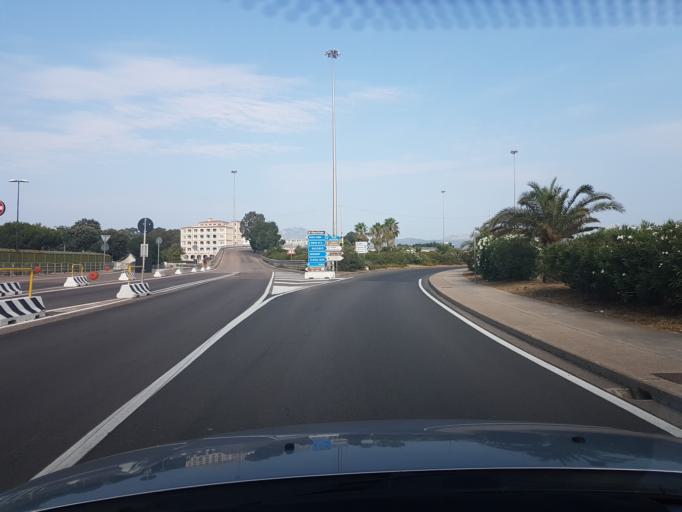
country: IT
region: Sardinia
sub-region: Provincia di Olbia-Tempio
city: Olbia
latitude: 40.9248
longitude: 9.5102
